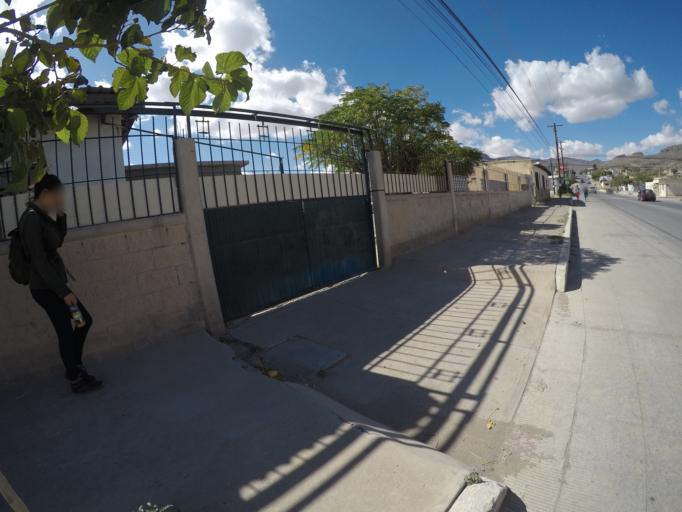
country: MX
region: Chihuahua
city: Ciudad Juarez
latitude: 31.6896
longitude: -106.4834
